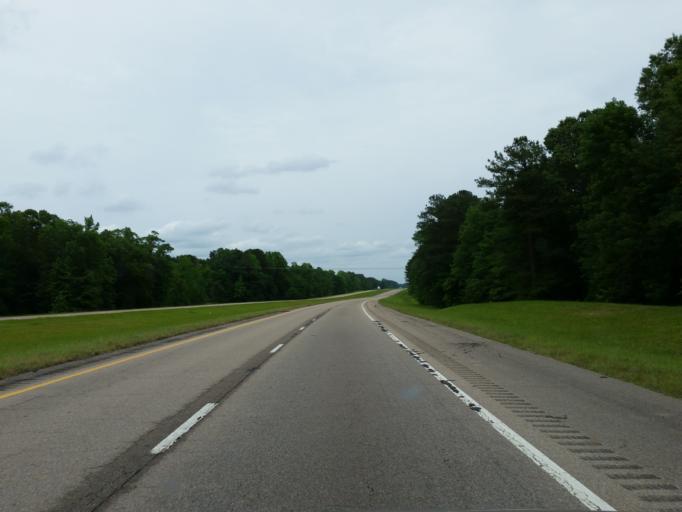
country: US
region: Mississippi
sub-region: Clarke County
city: Stonewall
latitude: 31.9905
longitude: -88.9458
